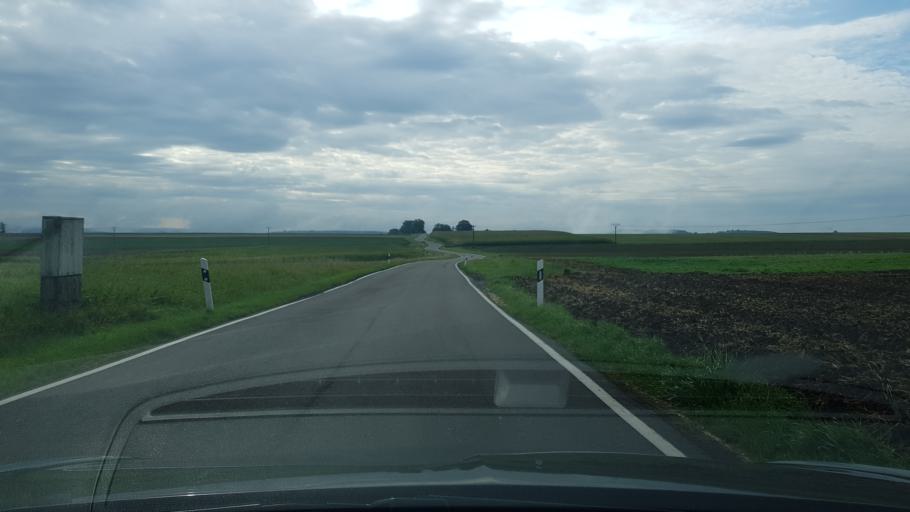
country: DE
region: Rheinland-Pfalz
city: Munstermaifeld
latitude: 50.2369
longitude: 7.3838
